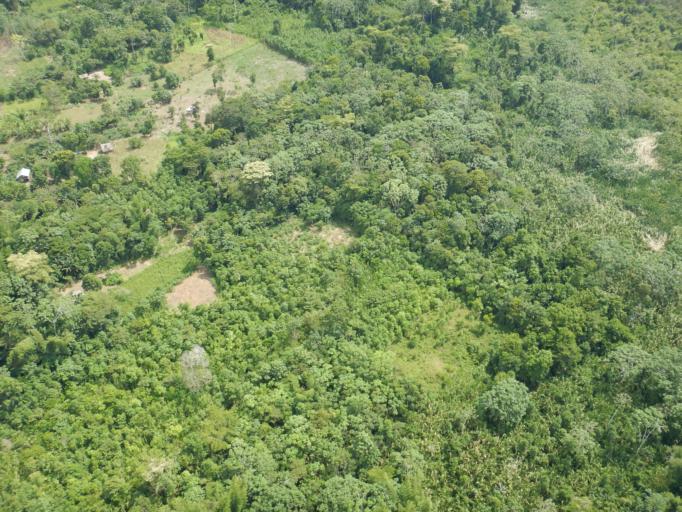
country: BO
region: Cochabamba
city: Chimore
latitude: -17.0003
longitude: -64.6941
